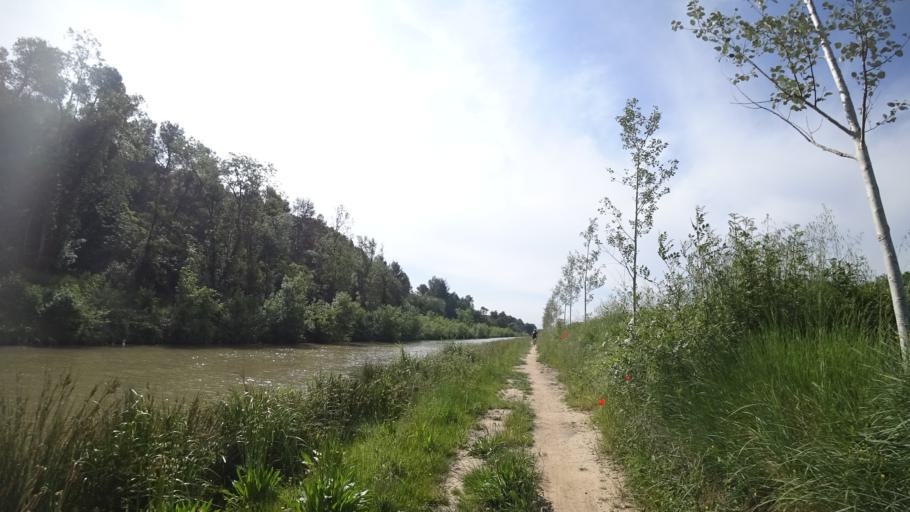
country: FR
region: Languedoc-Roussillon
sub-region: Departement de l'Herault
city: Olonzac
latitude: 43.2554
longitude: 2.7534
